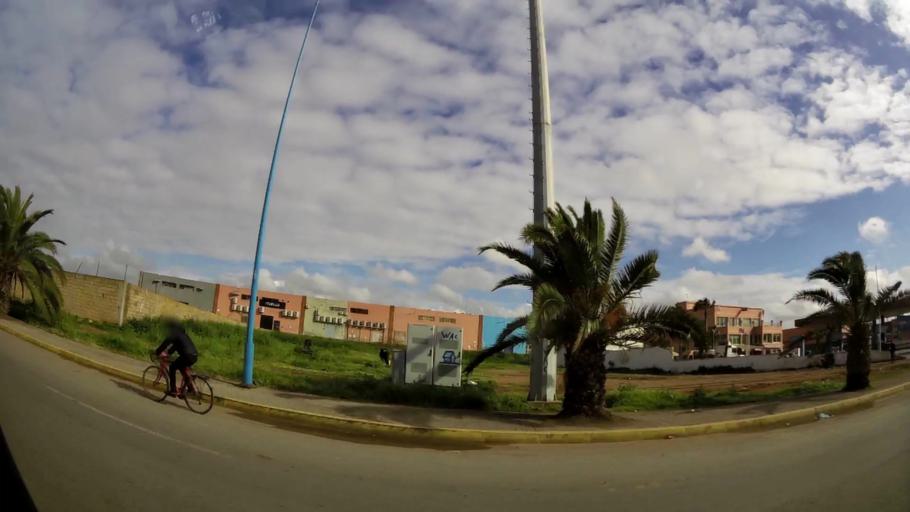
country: MA
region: Grand Casablanca
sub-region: Mohammedia
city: Mohammedia
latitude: 33.7098
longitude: -7.3486
